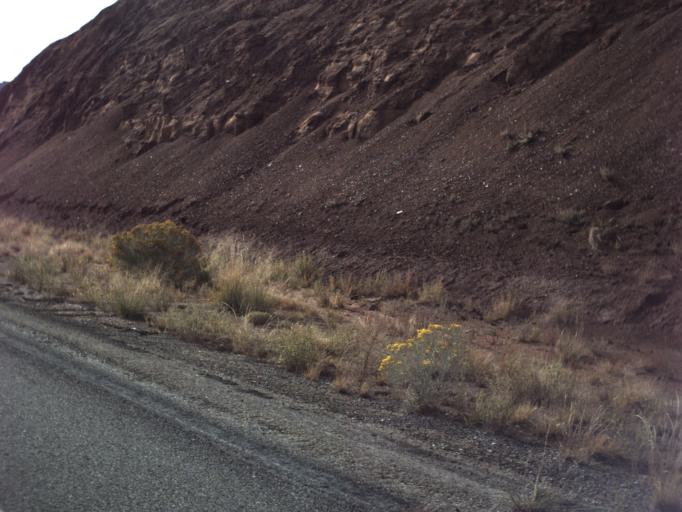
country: US
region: Utah
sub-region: Emery County
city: Ferron
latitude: 38.8402
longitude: -111.0693
